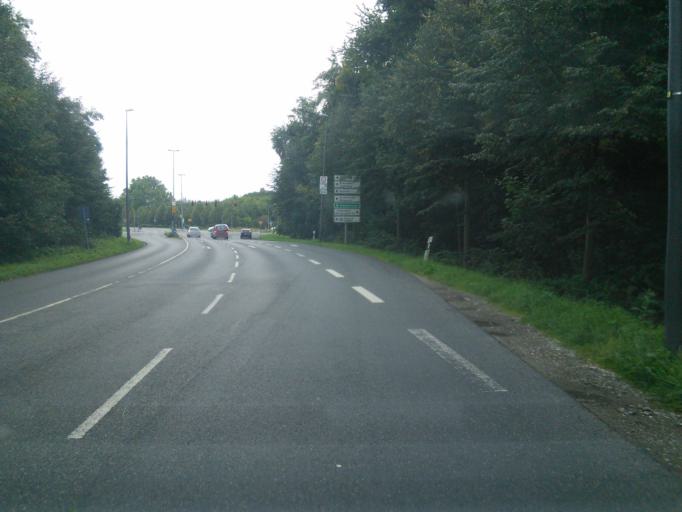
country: DE
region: North Rhine-Westphalia
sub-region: Regierungsbezirk Koln
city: Mengenich
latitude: 50.9691
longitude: 6.8678
